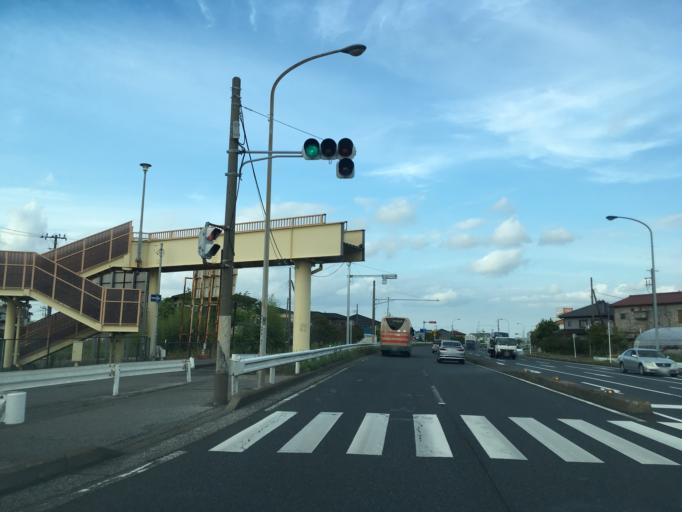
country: JP
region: Chiba
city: Kisarazu
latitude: 35.4066
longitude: 139.9450
